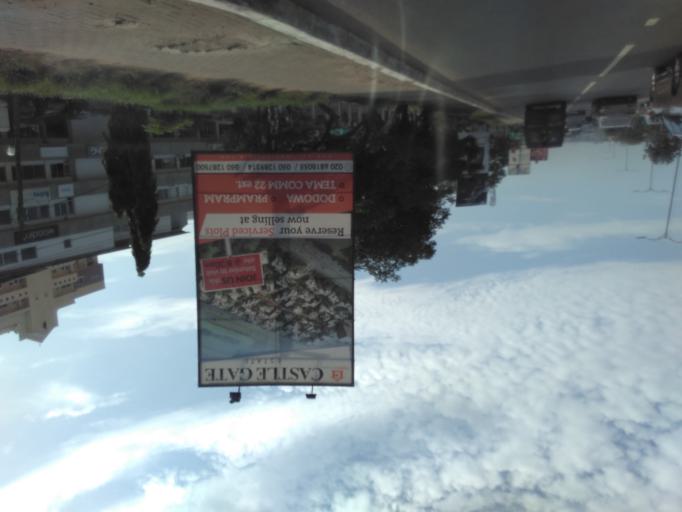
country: GH
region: Greater Accra
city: Medina Estates
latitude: 5.6150
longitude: -0.1758
